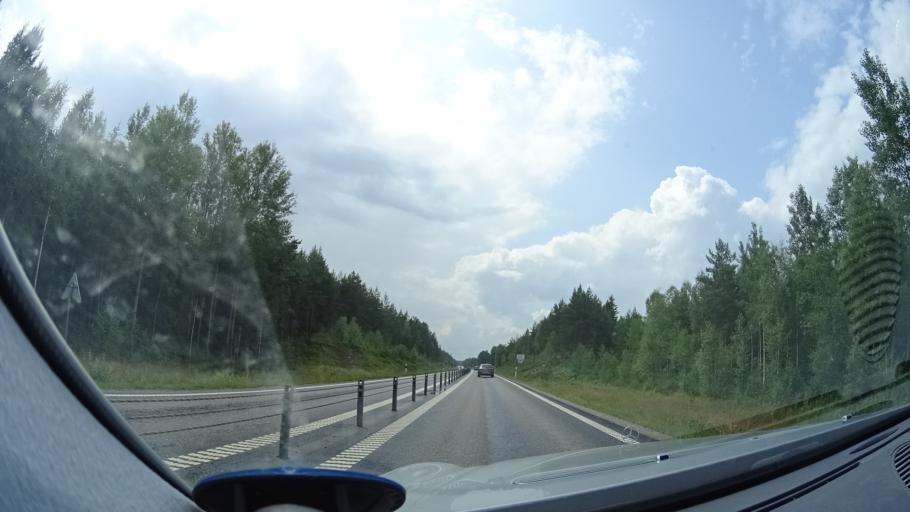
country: SE
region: Kalmar
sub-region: Nybro Kommun
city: Nybro
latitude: 56.7196
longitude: 15.7888
